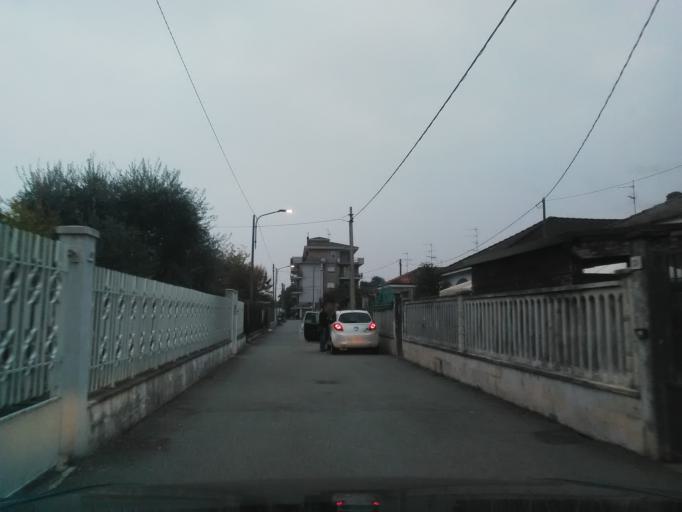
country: IT
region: Piedmont
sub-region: Provincia di Vercelli
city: Santhia
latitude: 45.3708
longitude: 8.1662
